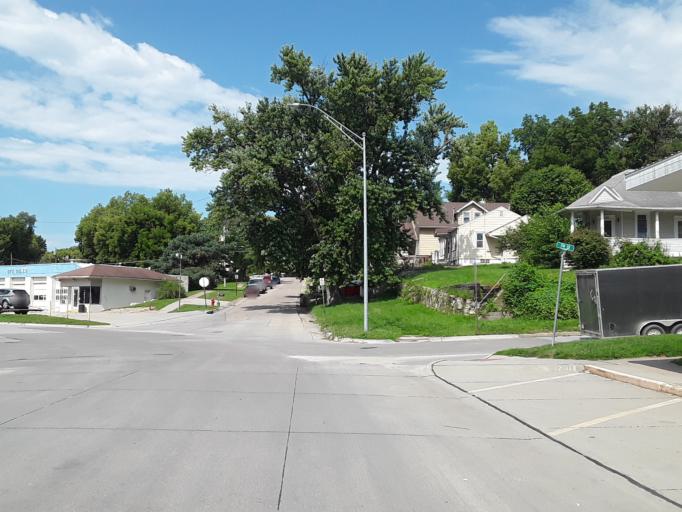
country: US
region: Nebraska
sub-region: Cass County
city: Plattsmouth
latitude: 41.0102
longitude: -95.8871
